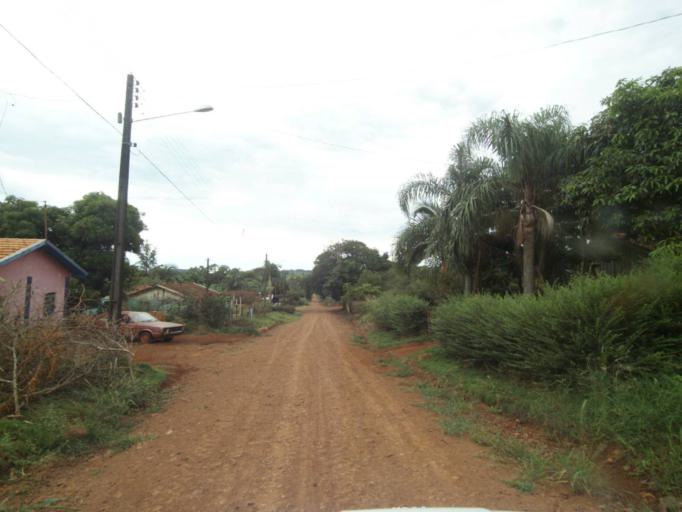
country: BR
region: Parana
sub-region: Guaraniacu
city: Guaraniacu
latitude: -24.9218
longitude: -52.9396
